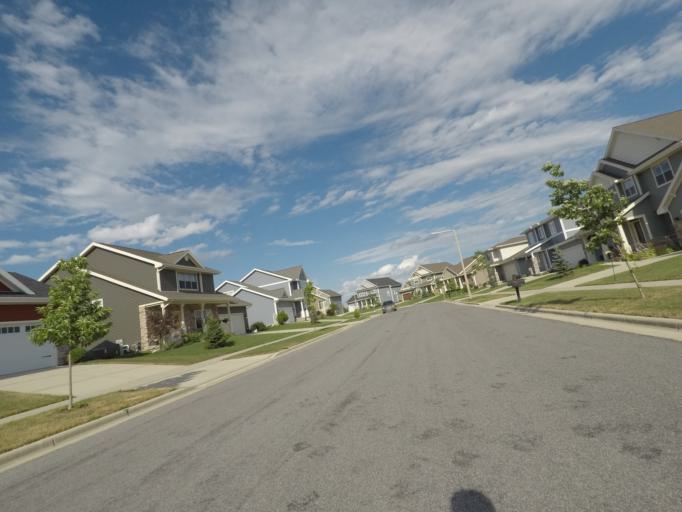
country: US
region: Wisconsin
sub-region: Dane County
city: Middleton
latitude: 43.0682
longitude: -89.5585
